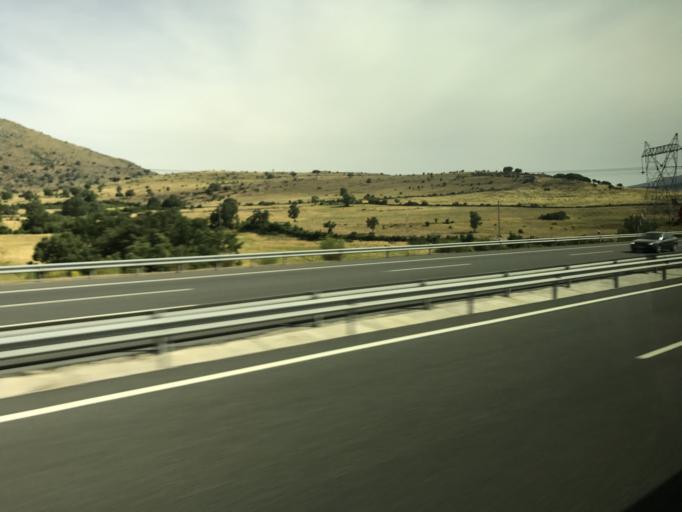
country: ES
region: Castille and Leon
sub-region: Provincia de Segovia
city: Vegas de Matute
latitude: 40.7388
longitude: -4.2612
